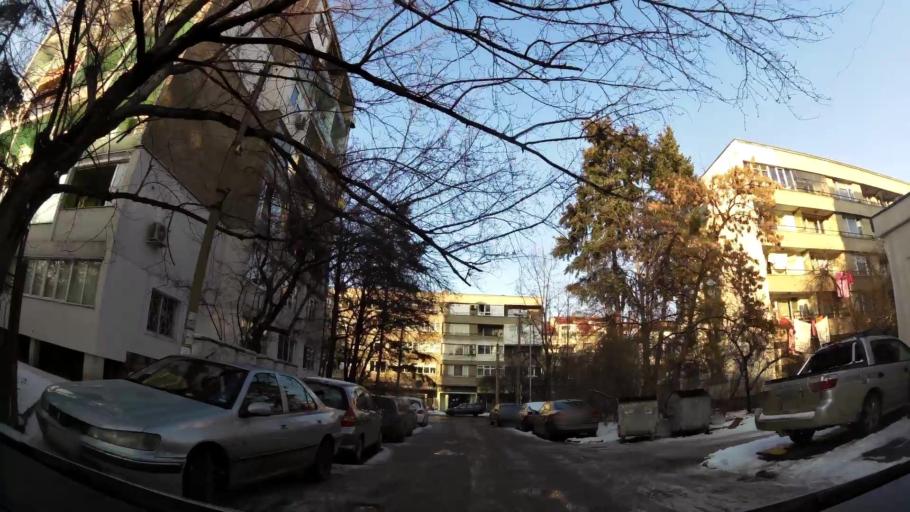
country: BG
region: Sofia-Capital
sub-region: Stolichna Obshtina
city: Sofia
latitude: 42.6824
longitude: 23.3644
